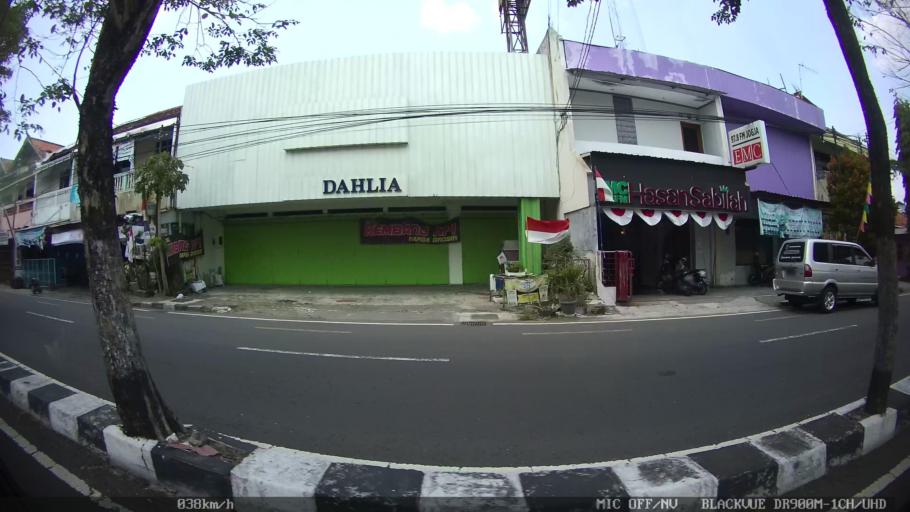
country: ID
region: Daerah Istimewa Yogyakarta
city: Yogyakarta
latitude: -7.8175
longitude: 110.3875
